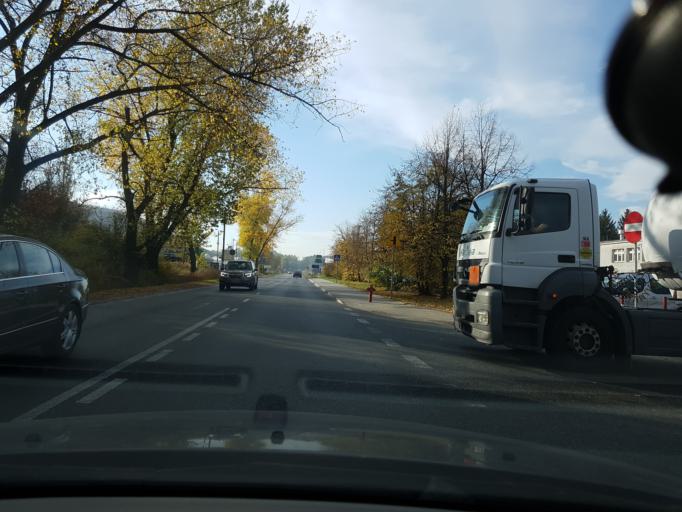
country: PL
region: Masovian Voivodeship
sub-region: Powiat warszawski zachodni
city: Babice
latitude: 52.2814
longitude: 20.8759
